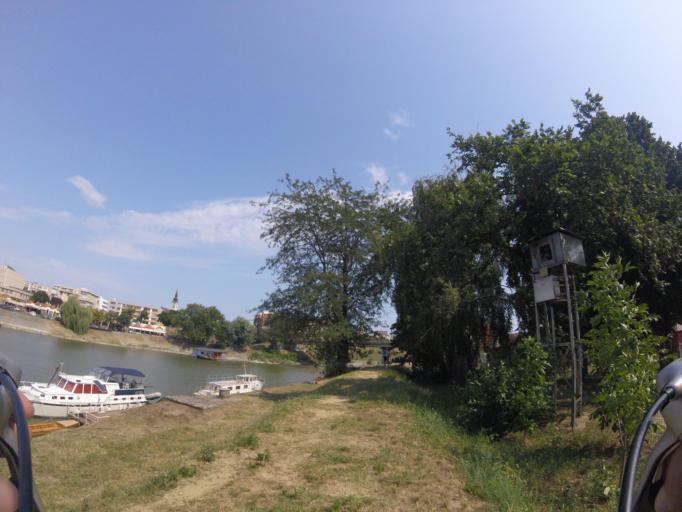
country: HU
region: Bacs-Kiskun
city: Baja
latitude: 46.1786
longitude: 18.9472
